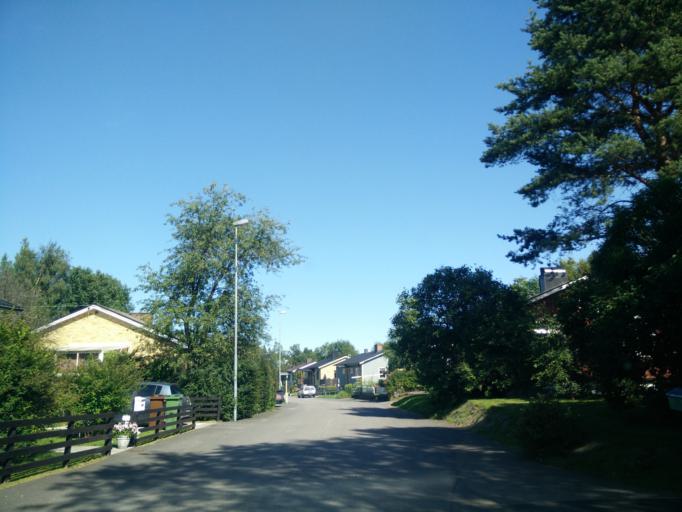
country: SE
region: Vaesternorrland
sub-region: Haernoesands Kommun
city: Haernoesand
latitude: 62.6352
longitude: 17.9127
